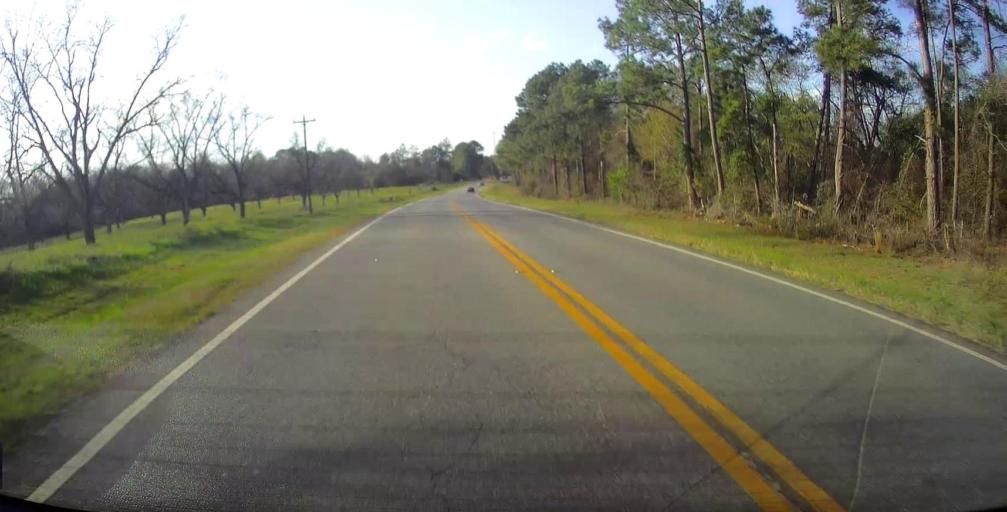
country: US
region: Georgia
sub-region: Toombs County
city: Lyons
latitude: 32.1481
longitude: -82.2616
